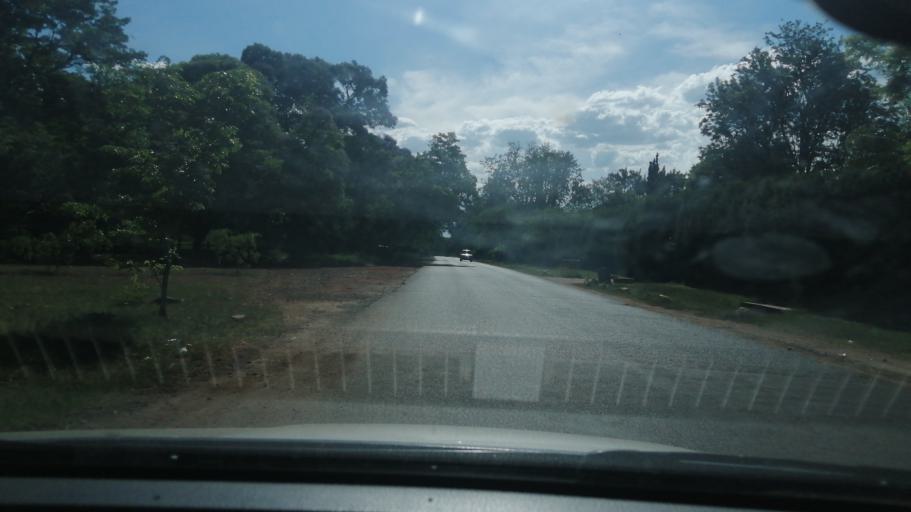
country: ZW
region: Harare
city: Harare
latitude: -17.7944
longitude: 31.0568
